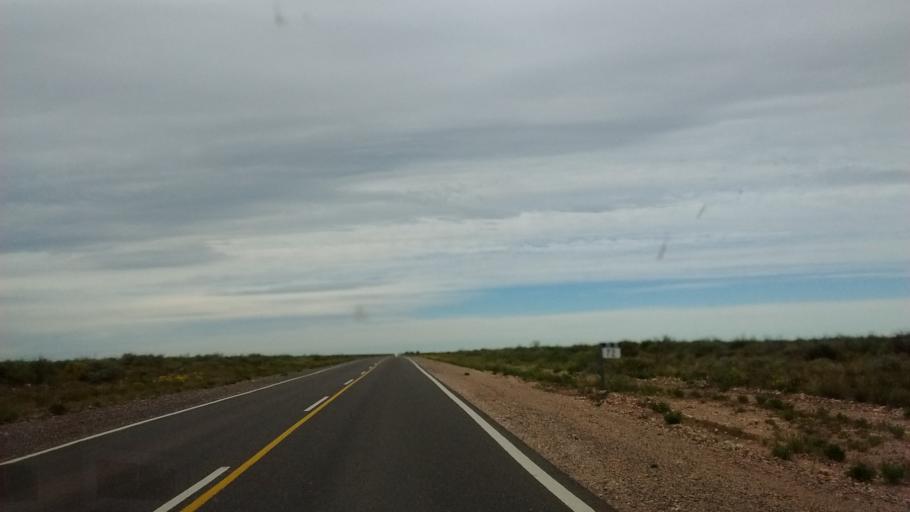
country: AR
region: Rio Negro
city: Contraalmirante Cordero
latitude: -38.3635
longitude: -68.0185
